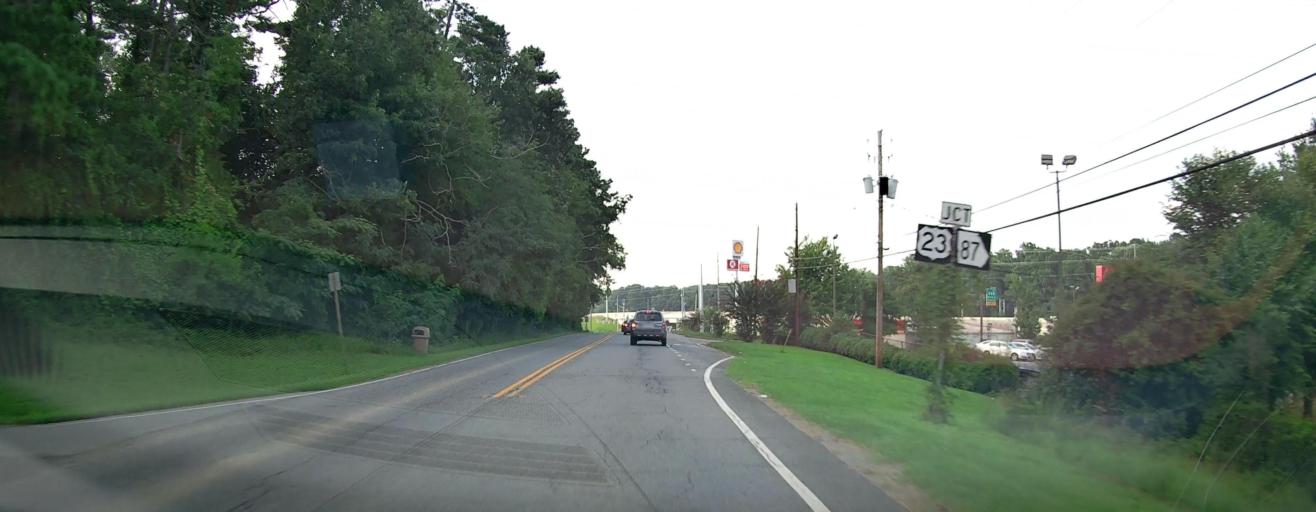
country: US
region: Georgia
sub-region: Bibb County
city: Macon
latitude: 32.8711
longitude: -83.6624
